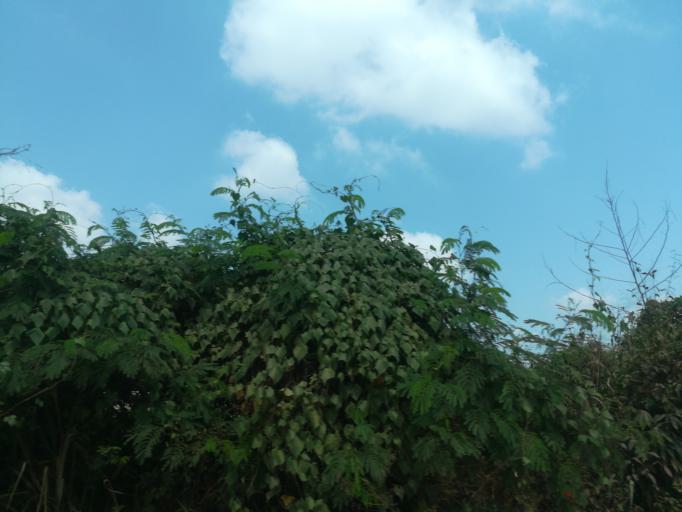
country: NG
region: Ogun
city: Abeokuta
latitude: 7.1396
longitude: 3.4097
